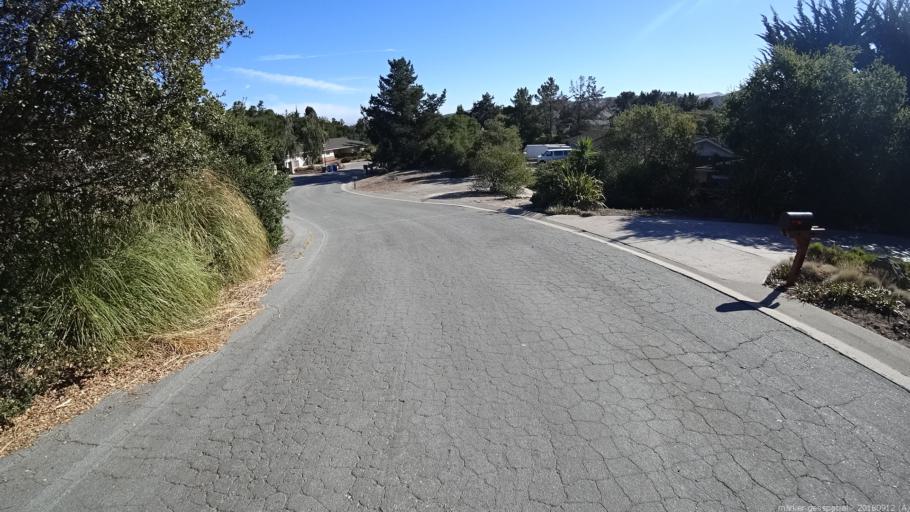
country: US
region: California
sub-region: Monterey County
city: Carmel Valley Village
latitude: 36.5639
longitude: -121.7347
